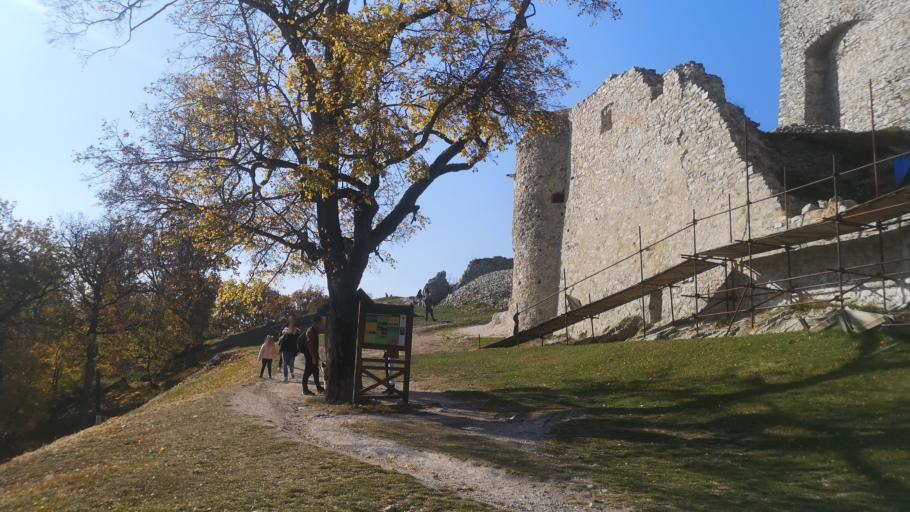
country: SK
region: Nitriansky
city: Zlate Moravce
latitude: 48.4786
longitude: 18.4264
